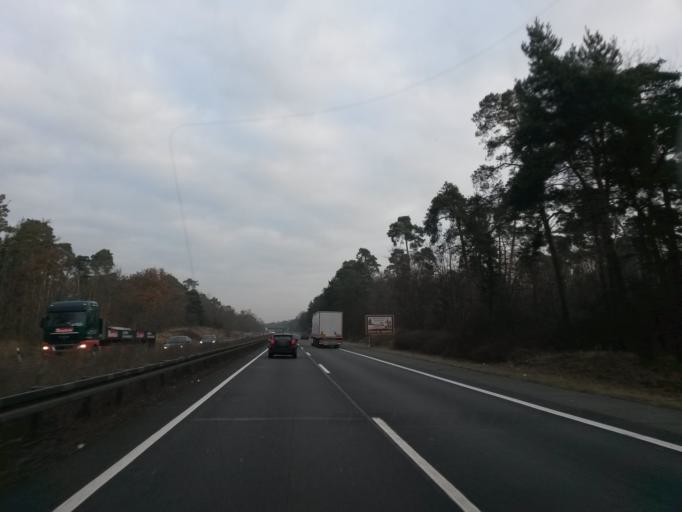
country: DE
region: Hesse
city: Pfungstadt
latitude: 49.8270
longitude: 8.5881
